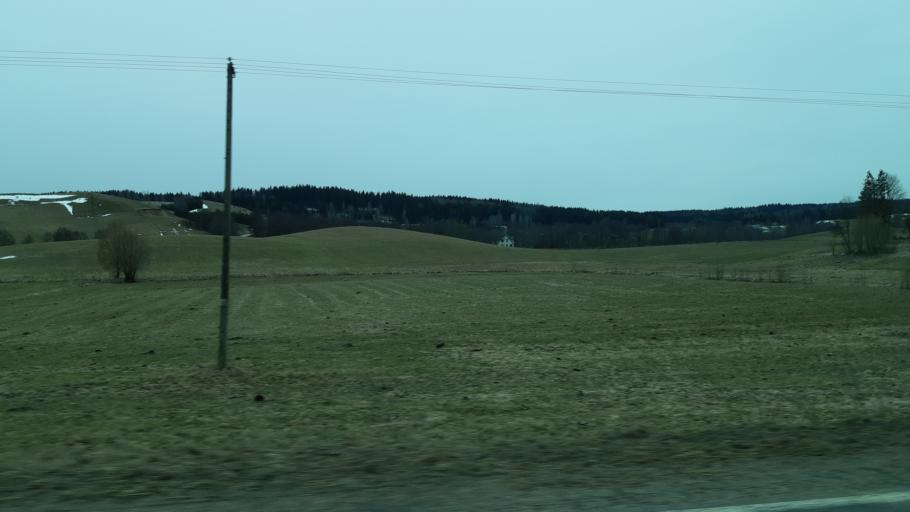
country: PL
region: Podlasie
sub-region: Suwalki
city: Suwalki
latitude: 54.3349
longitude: 22.9311
